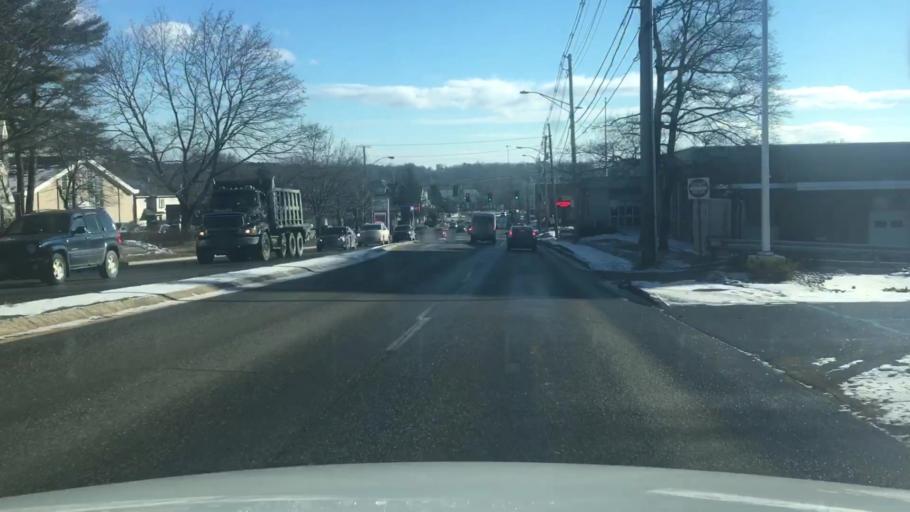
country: US
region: Maine
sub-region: Kennebec County
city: Augusta
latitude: 44.3113
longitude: -69.7845
